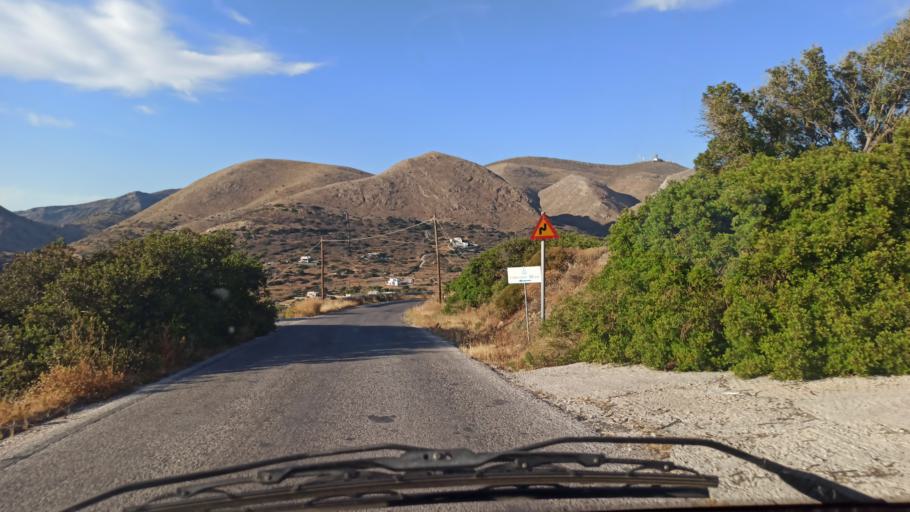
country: GR
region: South Aegean
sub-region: Nomos Kykladon
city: Ano Syros
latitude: 37.4415
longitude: 24.9026
